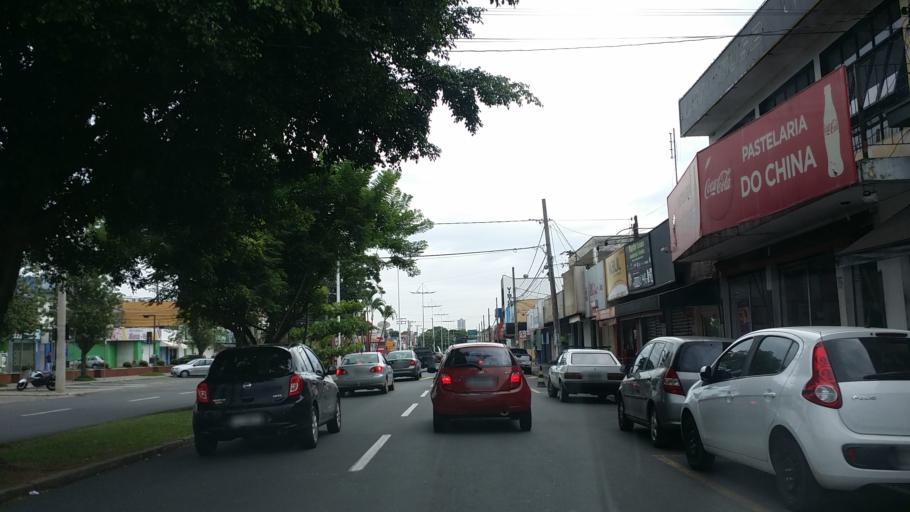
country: BR
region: Sao Paulo
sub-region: Indaiatuba
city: Indaiatuba
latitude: -23.1033
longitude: -47.2170
